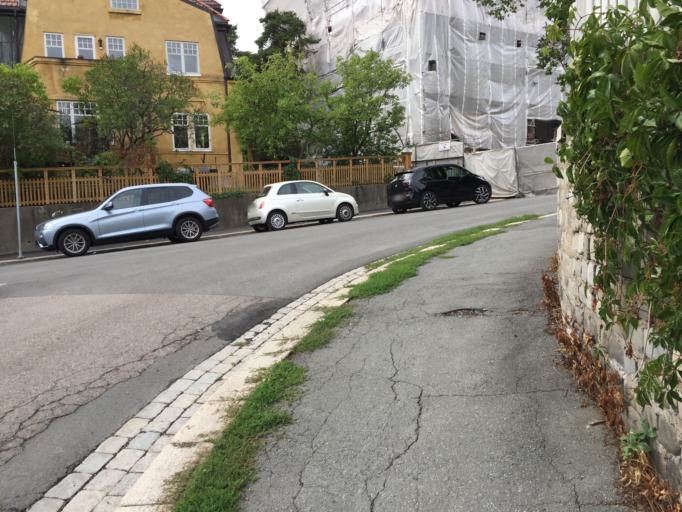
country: NO
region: Oslo
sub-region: Oslo
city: Sjolyststranda
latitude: 59.9165
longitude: 10.7069
